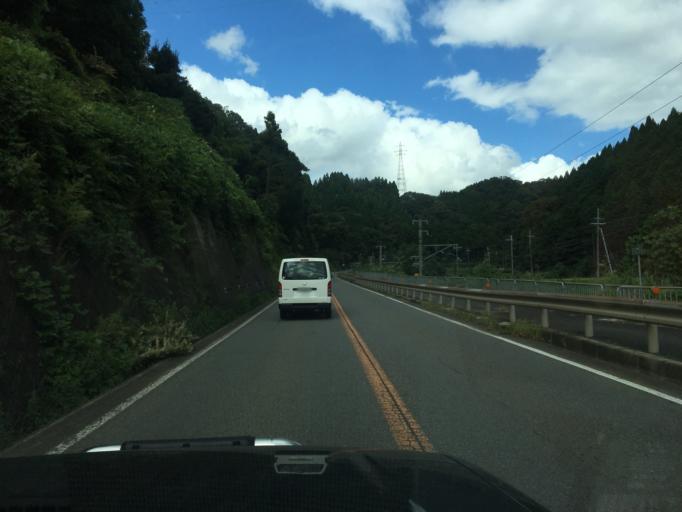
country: JP
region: Kyoto
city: Fukuchiyama
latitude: 35.3326
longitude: 134.9124
